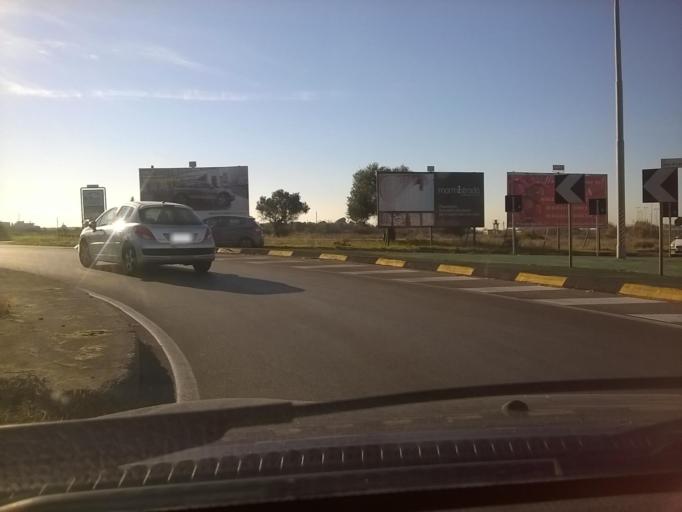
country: IT
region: Apulia
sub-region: Provincia di Taranto
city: Taranto
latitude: 40.4404
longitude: 17.2557
